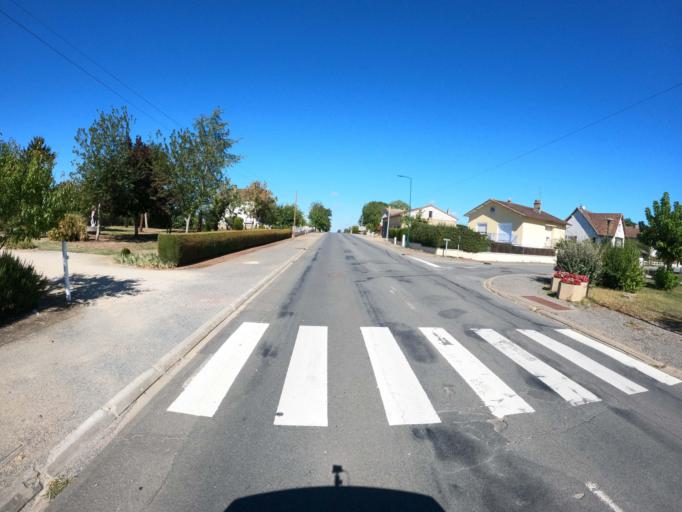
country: FR
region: Poitou-Charentes
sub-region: Departement de la Vienne
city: Lathus-Saint-Remy
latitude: 46.3382
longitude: 0.9554
